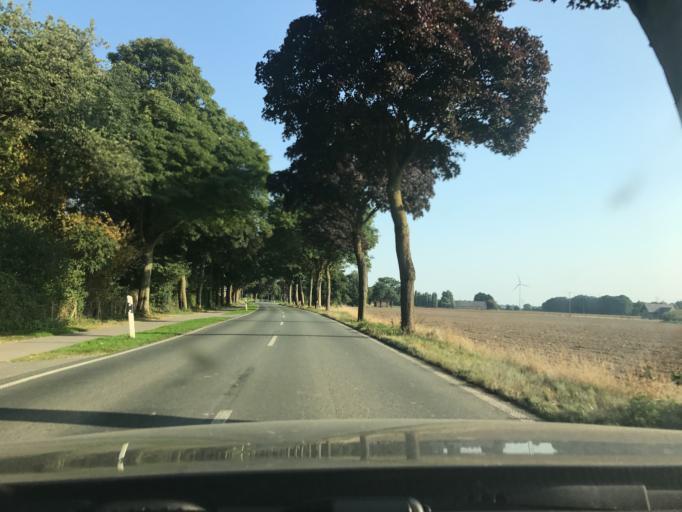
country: DE
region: North Rhine-Westphalia
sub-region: Regierungsbezirk Dusseldorf
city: Kleve
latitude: 51.7428
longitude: 6.1970
